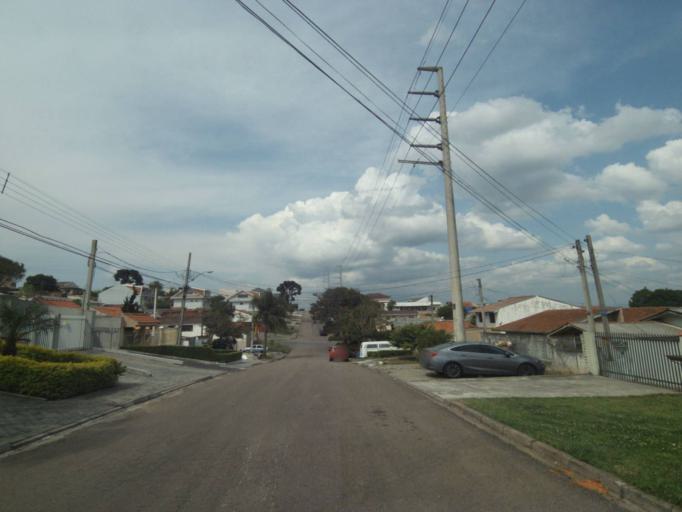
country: BR
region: Parana
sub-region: Pinhais
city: Pinhais
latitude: -25.4011
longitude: -49.1970
